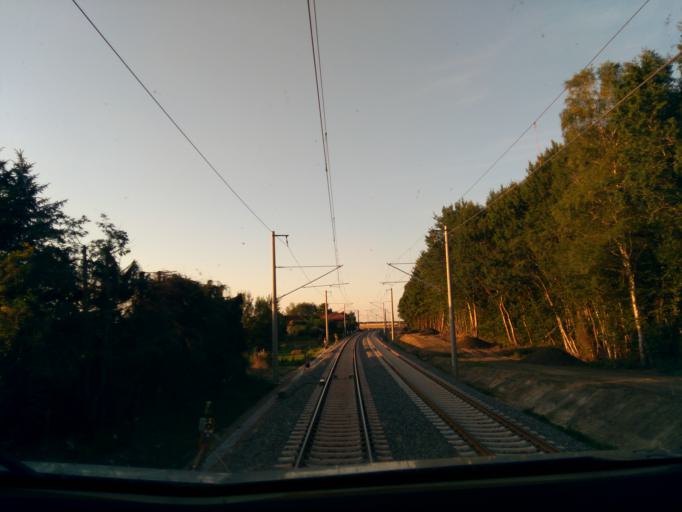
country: DE
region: Mecklenburg-Vorpommern
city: Lubstorf
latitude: 53.7371
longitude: 11.4153
